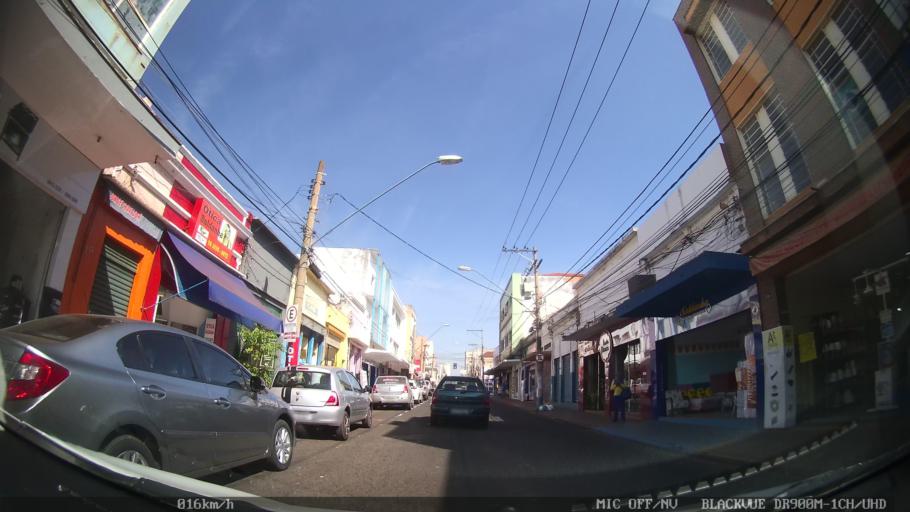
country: BR
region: Sao Paulo
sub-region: Ribeirao Preto
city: Ribeirao Preto
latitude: -21.1723
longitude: -47.8101
